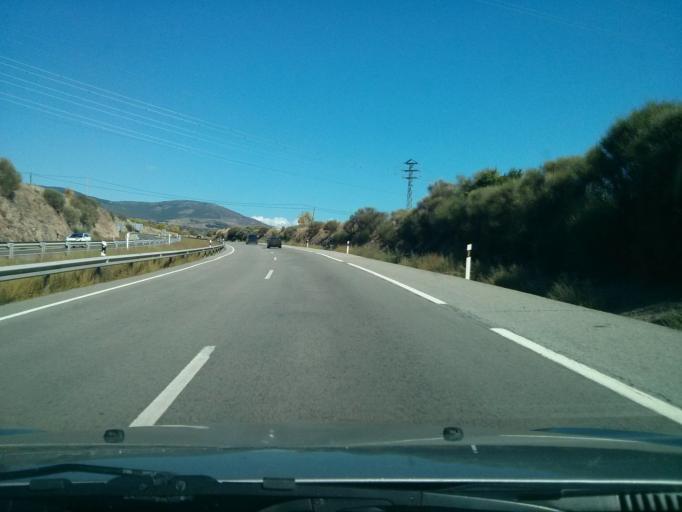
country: ES
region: Madrid
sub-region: Provincia de Madrid
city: Buitrago del Lozoya
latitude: 41.0024
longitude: -3.6374
